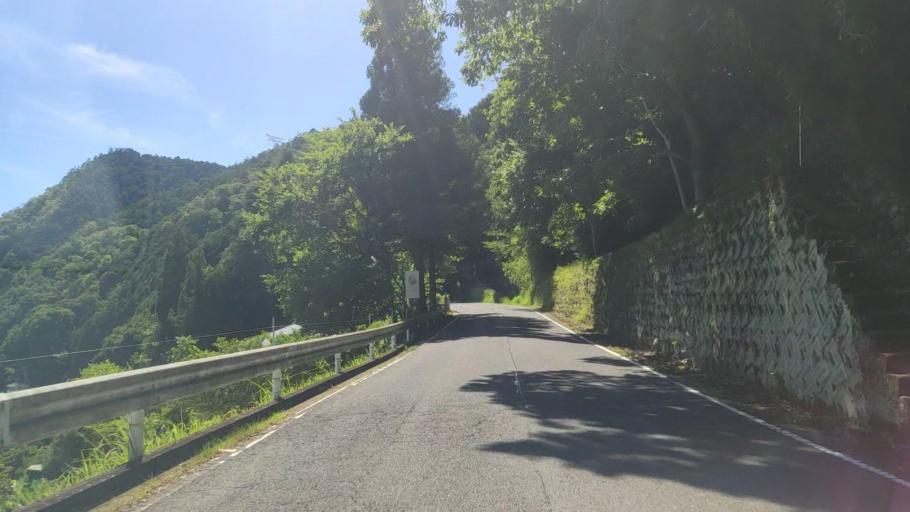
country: JP
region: Nara
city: Yoshino-cho
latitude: 34.3935
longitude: 135.9256
